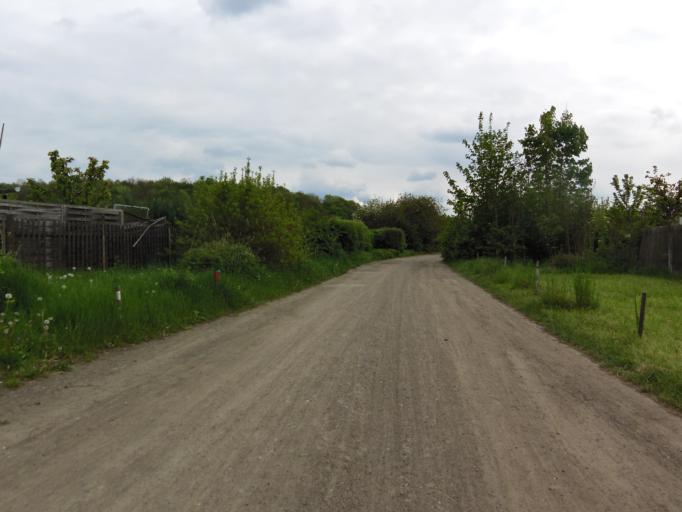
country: DE
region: Saxony
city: Markkleeberg
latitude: 51.3079
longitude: 12.3345
